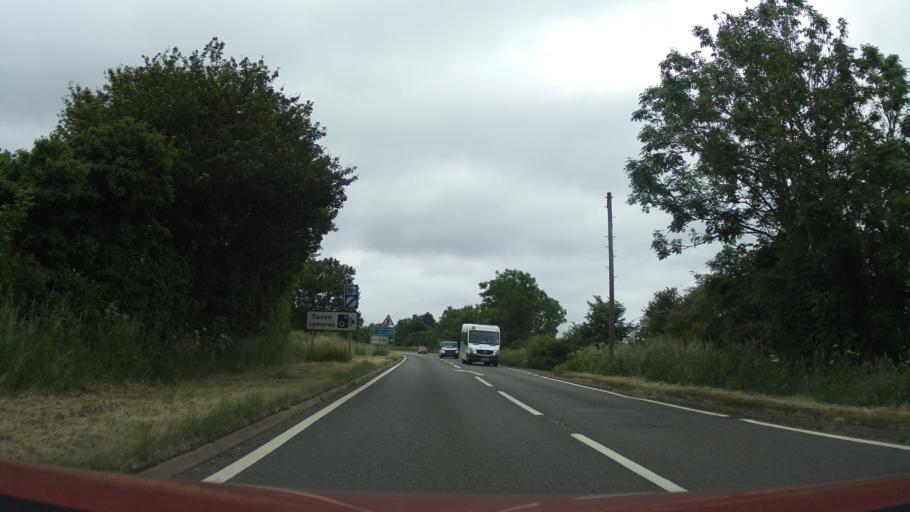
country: GB
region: England
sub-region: Leicestershire
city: Houghton on the Hill
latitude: 52.6212
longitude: -0.9619
